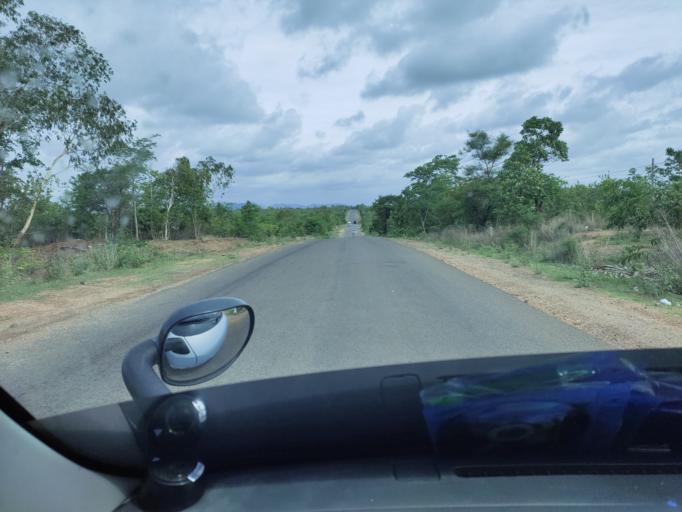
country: MM
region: Magway
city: Chauk
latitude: 20.9705
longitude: 95.0560
